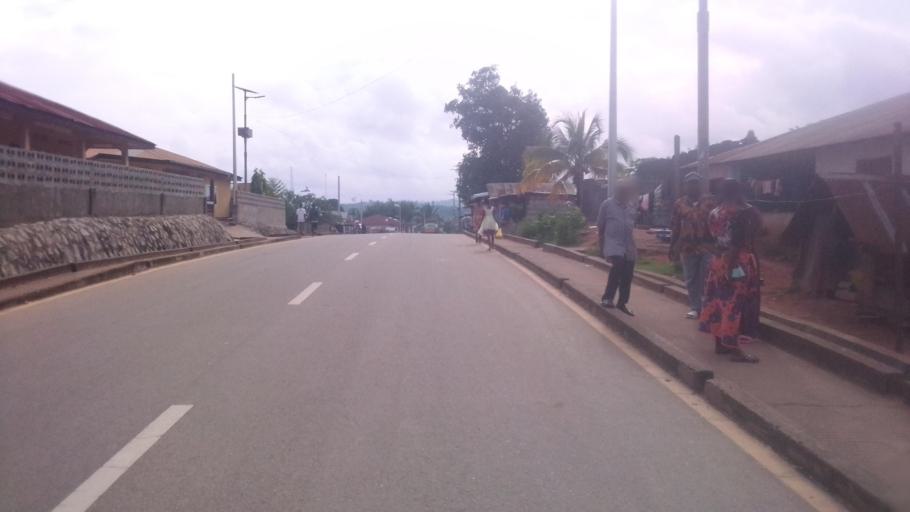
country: SL
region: Eastern Province
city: Kailahun
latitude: 8.2695
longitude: -10.5798
